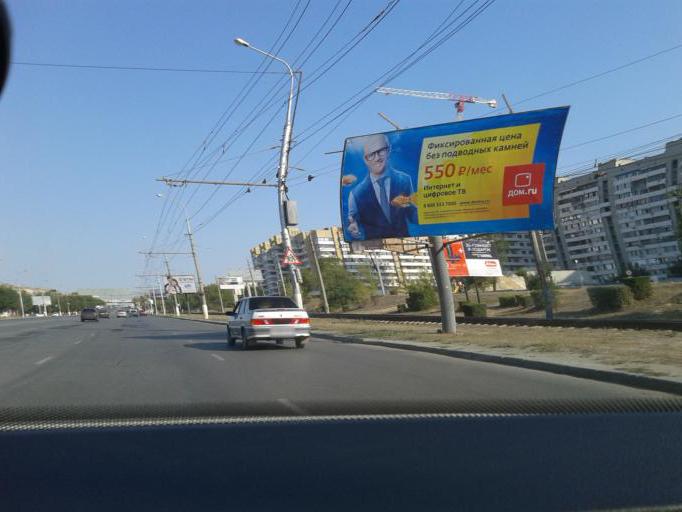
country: RU
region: Volgograd
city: Volgograd
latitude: 48.7468
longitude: 44.4874
